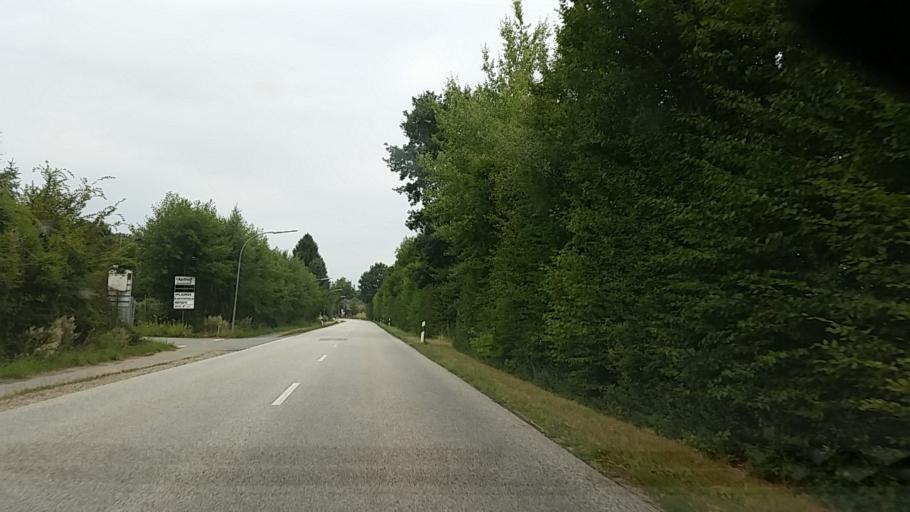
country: DE
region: Schleswig-Holstein
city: Hohenhorn
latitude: 53.4986
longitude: 10.3653
